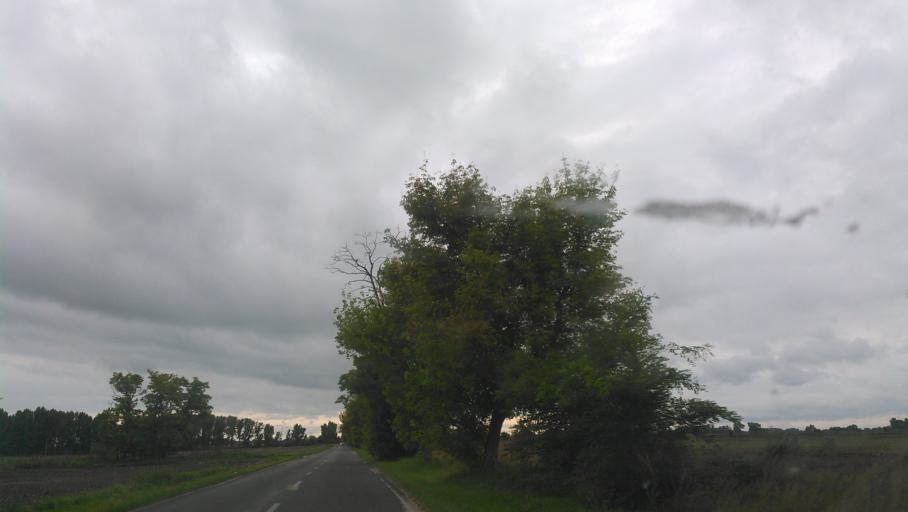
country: SK
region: Trnavsky
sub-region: Okres Dunajska Streda
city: Velky Meder
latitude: 47.9193
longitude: 17.7447
